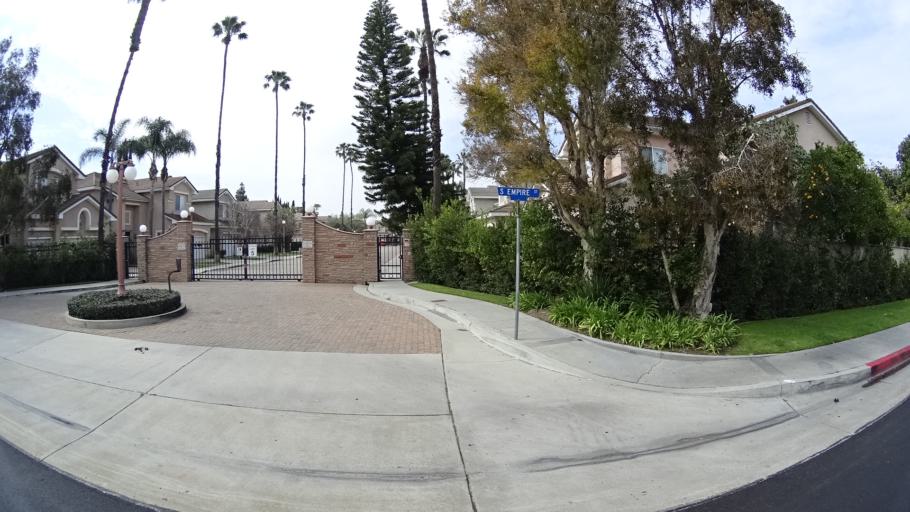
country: US
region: California
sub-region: Orange County
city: Stanton
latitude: 33.8157
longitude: -117.9546
